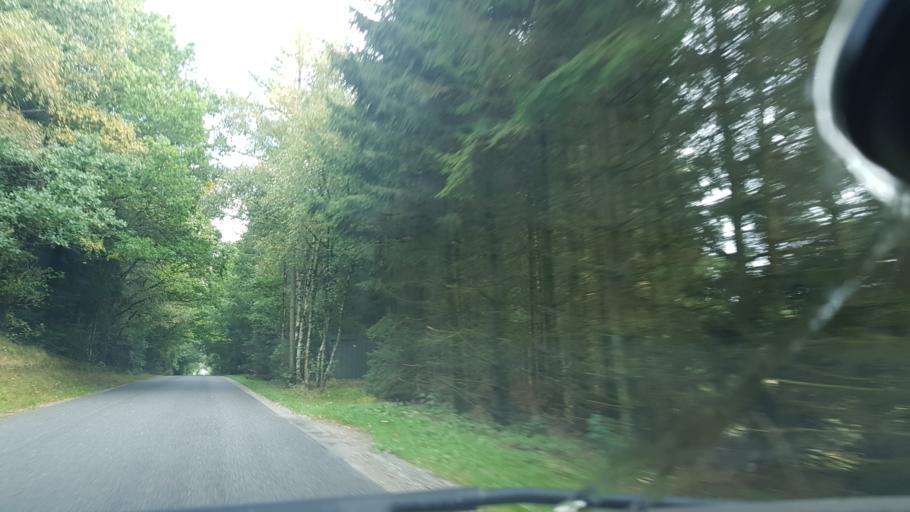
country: DK
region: South Denmark
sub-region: Billund Kommune
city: Billund
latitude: 55.6204
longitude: 9.0421
